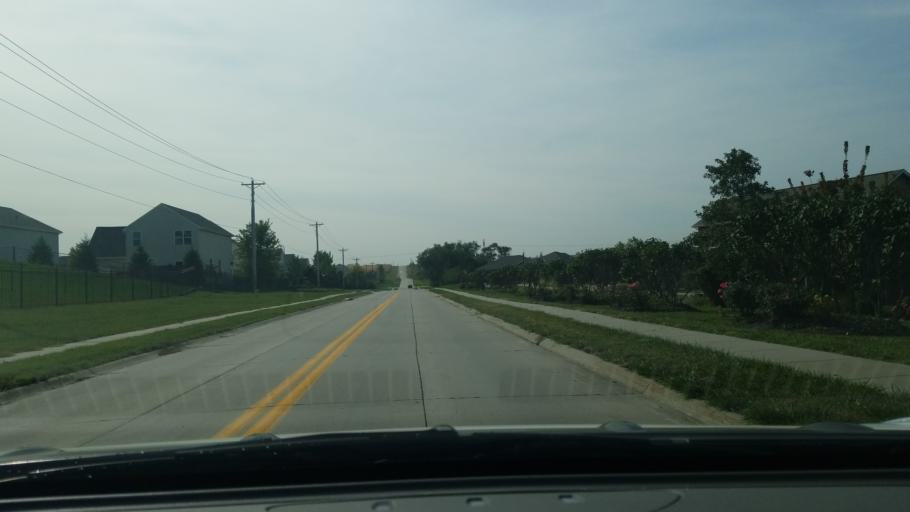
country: US
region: Nebraska
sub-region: Sarpy County
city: Papillion
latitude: 41.1296
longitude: -96.0621
